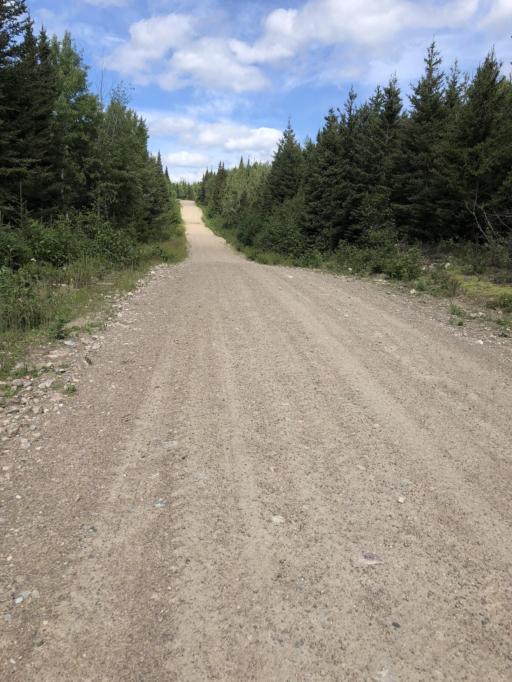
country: CA
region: Quebec
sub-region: Saguenay/Lac-Saint-Jean
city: Saguenay
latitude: 48.0199
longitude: -70.6586
